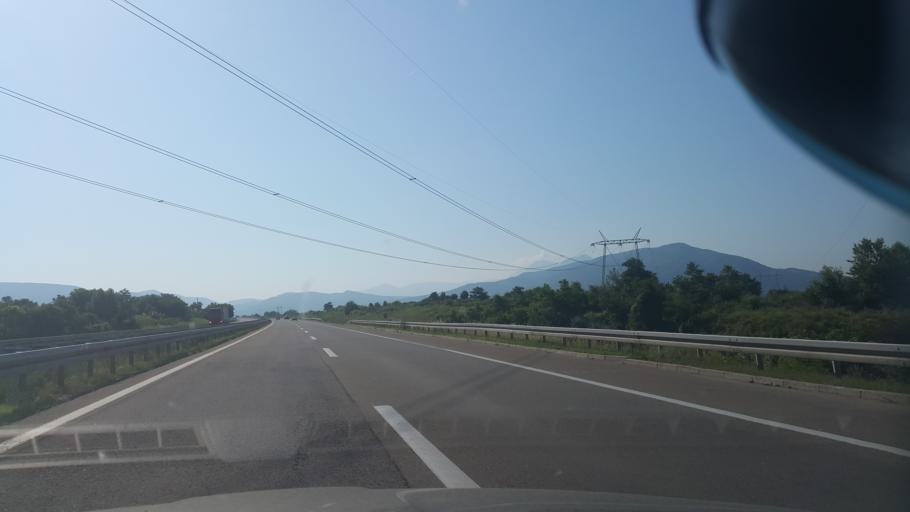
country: RS
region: Central Serbia
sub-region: Nisavski Okrug
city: Niska Banja
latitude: 43.3260
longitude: 21.9668
